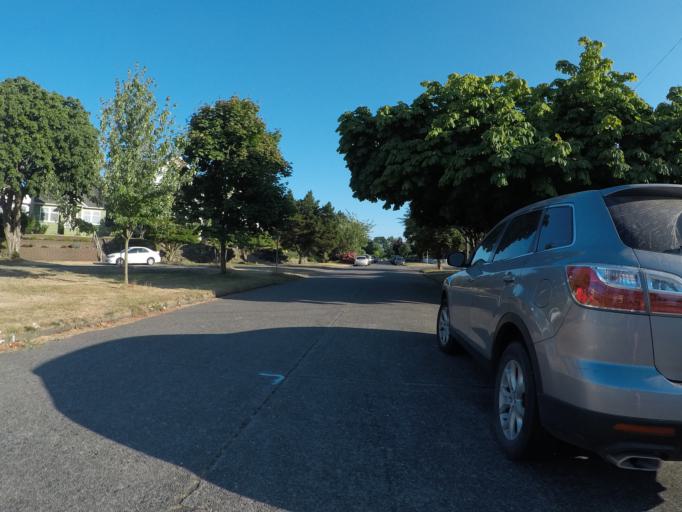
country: US
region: Washington
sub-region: King County
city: Seattle
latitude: 47.5853
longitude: -122.3877
